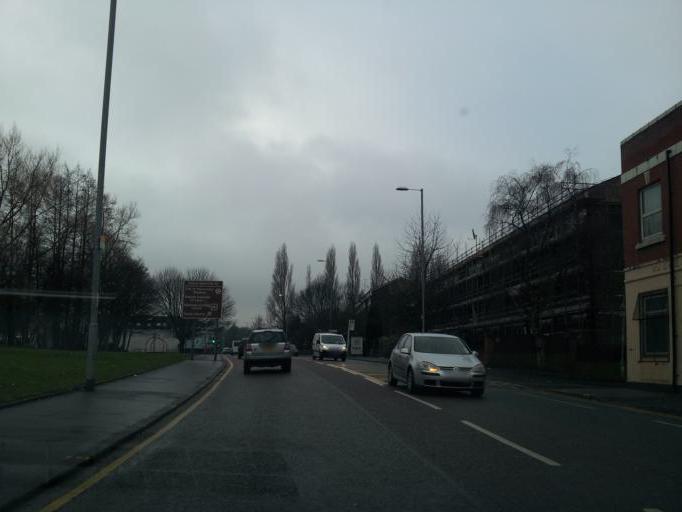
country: GB
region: England
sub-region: Manchester
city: Blackley
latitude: 53.5079
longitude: -2.2173
